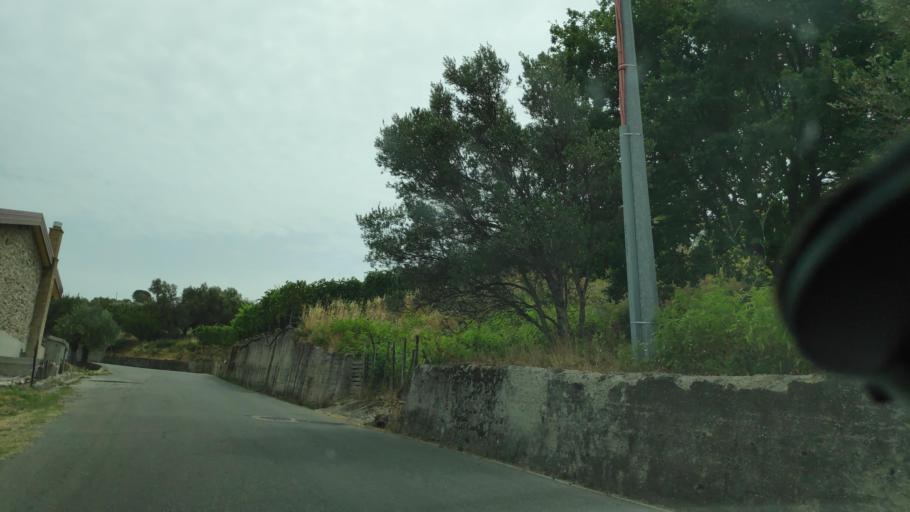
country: IT
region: Calabria
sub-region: Provincia di Catanzaro
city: Davoli
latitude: 38.6503
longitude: 16.4887
